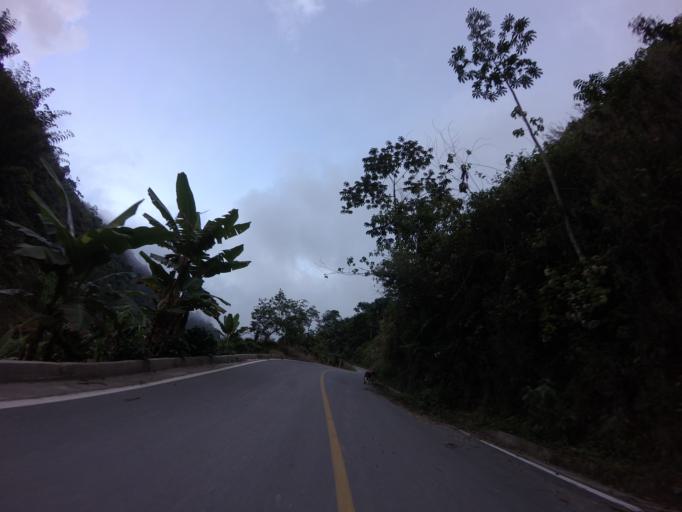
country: CO
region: Caldas
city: Manzanares
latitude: 5.3402
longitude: -75.1223
